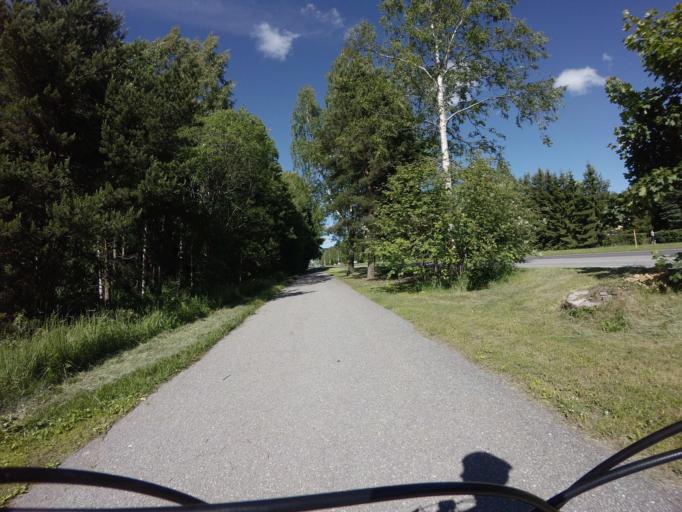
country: FI
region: Varsinais-Suomi
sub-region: Turku
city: Turku
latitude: 60.4861
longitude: 22.2755
